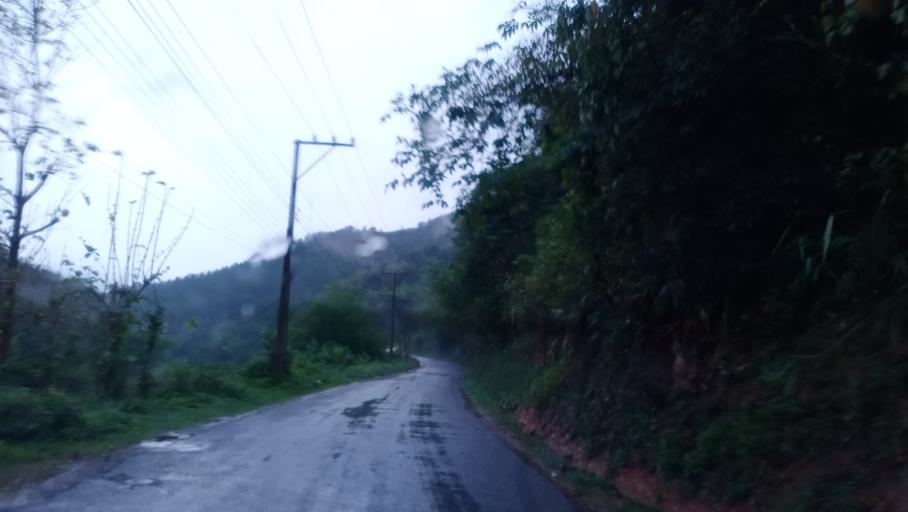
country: LA
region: Phongsali
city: Khoa
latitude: 21.0722
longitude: 102.4970
